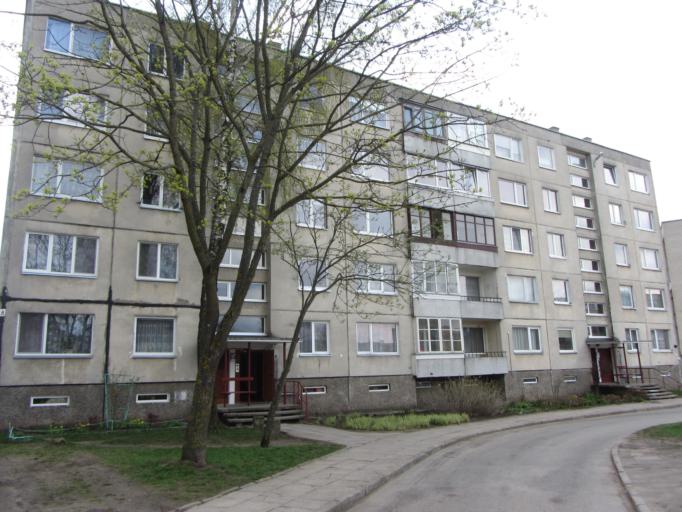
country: LT
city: Lentvaris
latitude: 54.6523
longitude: 25.0445
